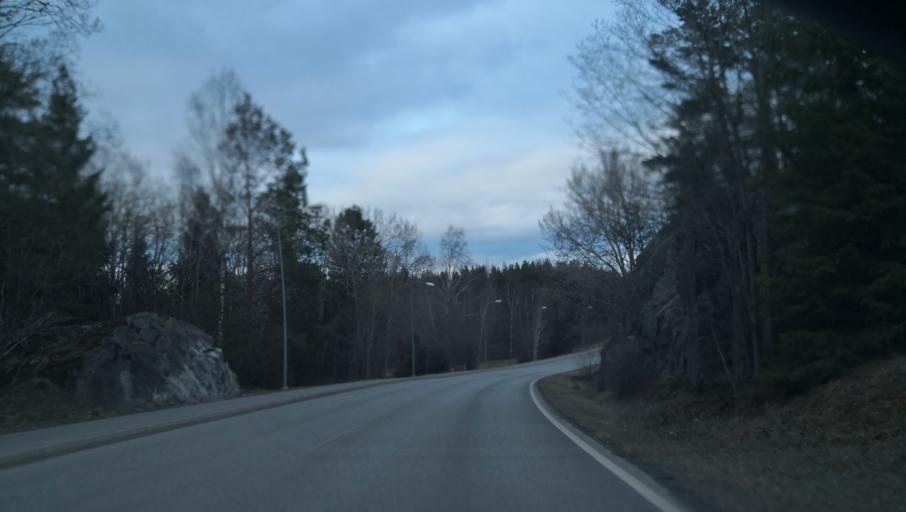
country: SE
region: Stockholm
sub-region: Varmdo Kommun
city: Gustavsberg
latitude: 59.3443
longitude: 18.3716
